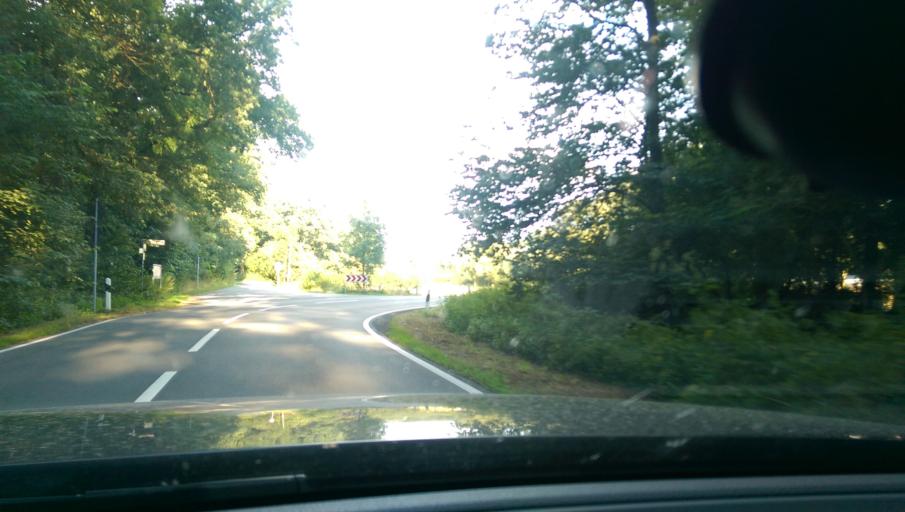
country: DE
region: Lower Saxony
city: Neustadt am Rubenberge
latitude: 52.5575
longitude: 9.5036
